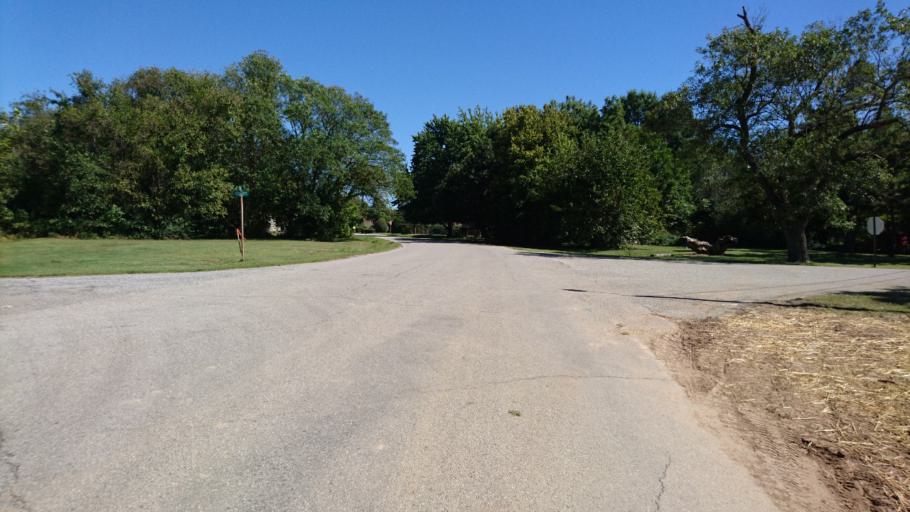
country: US
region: Kansas
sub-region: Cherokee County
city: Baxter Springs
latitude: 37.0333
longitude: -94.7383
